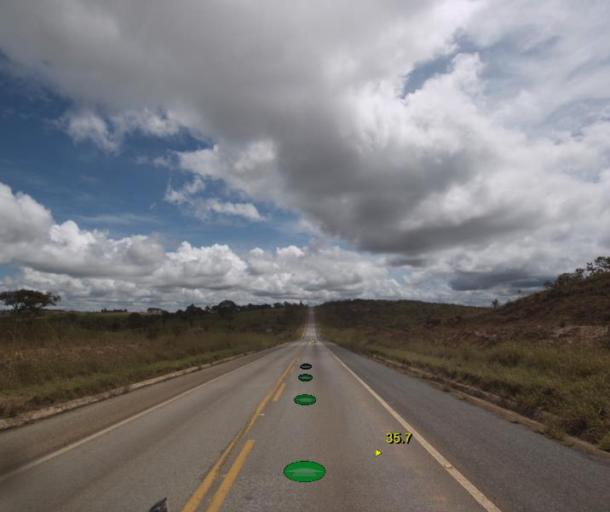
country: BR
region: Goias
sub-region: Pirenopolis
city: Pirenopolis
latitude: -15.7791
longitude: -48.4962
